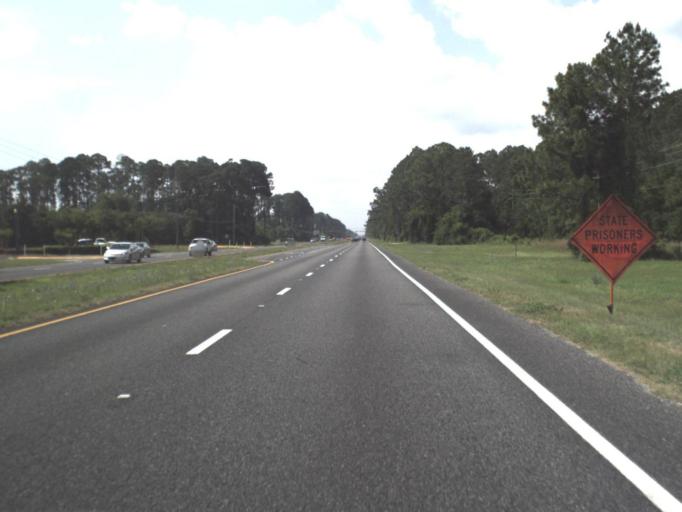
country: US
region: Florida
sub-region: Saint Johns County
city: Saint Augustine Shores
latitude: 29.8075
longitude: -81.3216
